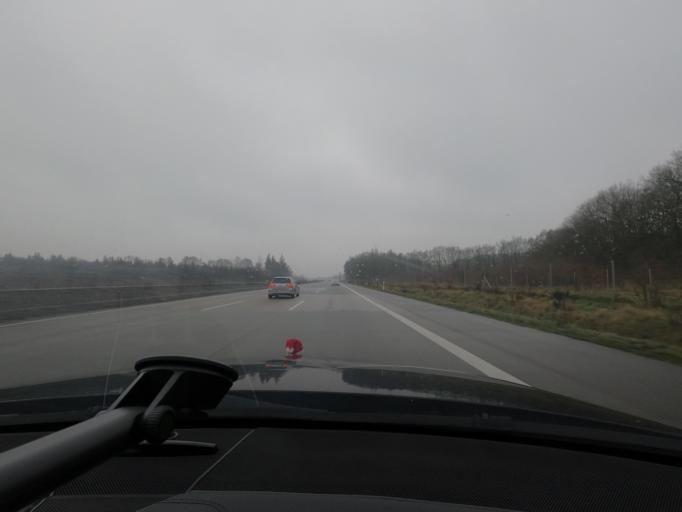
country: DE
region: Schleswig-Holstein
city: Bimohlen
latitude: 53.9274
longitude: 9.9411
